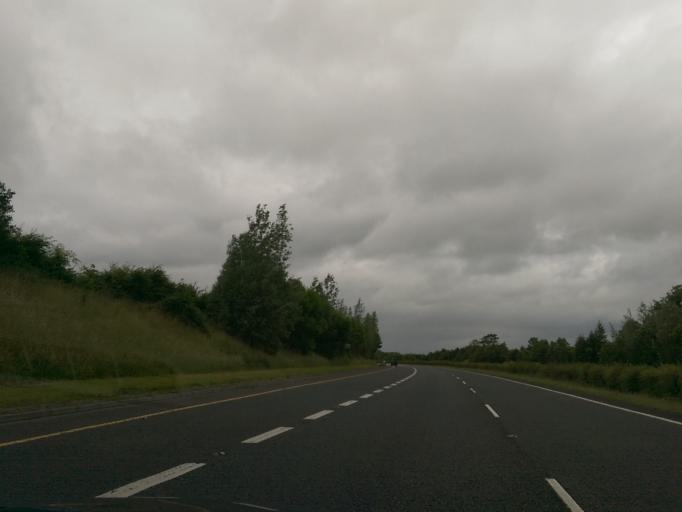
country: IE
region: Munster
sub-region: An Clar
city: Newmarket on Fergus
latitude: 52.7471
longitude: -8.8967
